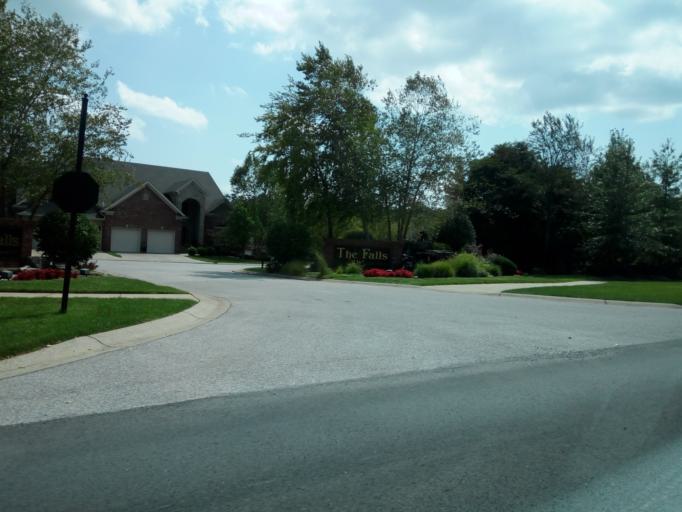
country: US
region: Kentucky
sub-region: Oldham County
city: Pewee Valley
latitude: 38.2815
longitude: -85.4860
